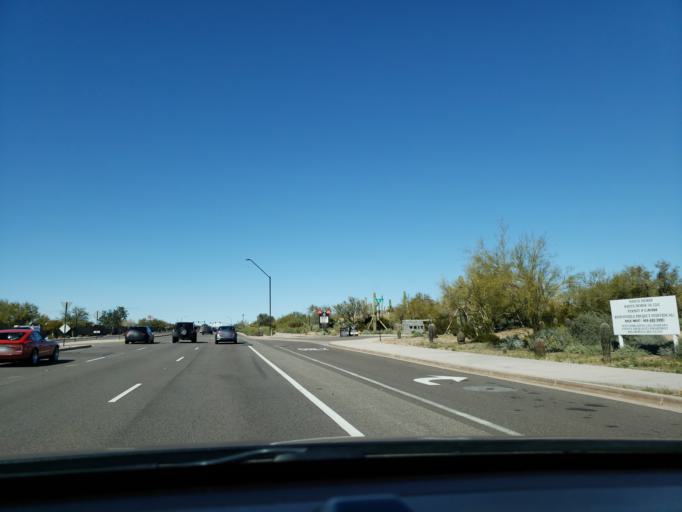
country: US
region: Arizona
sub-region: Maricopa County
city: Carefree
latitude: 33.6839
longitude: -111.8905
